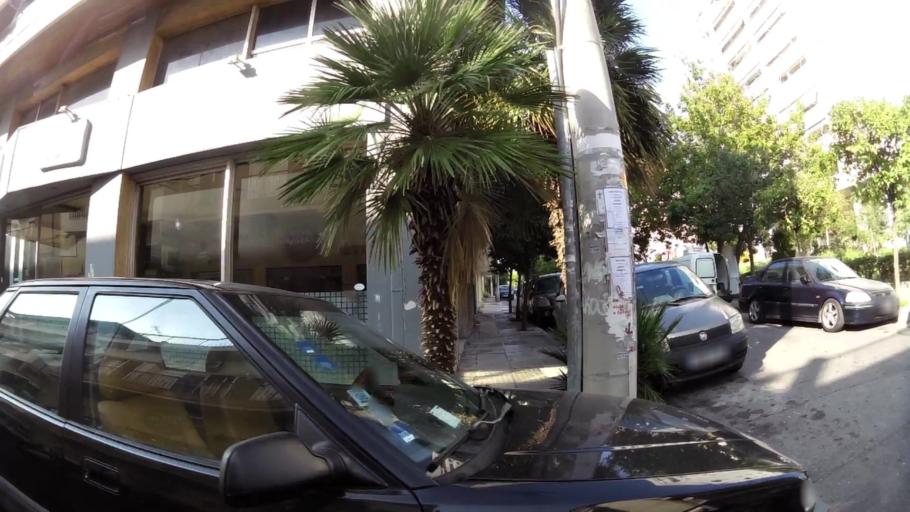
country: GR
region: Attica
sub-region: Nomos Piraios
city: Drapetsona
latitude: 37.9481
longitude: 23.6275
